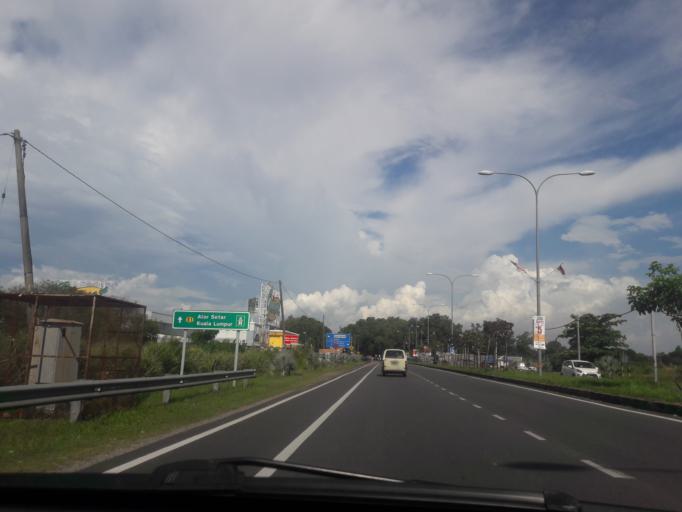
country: MY
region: Kedah
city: Sungai Petani
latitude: 5.6156
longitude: 100.4701
